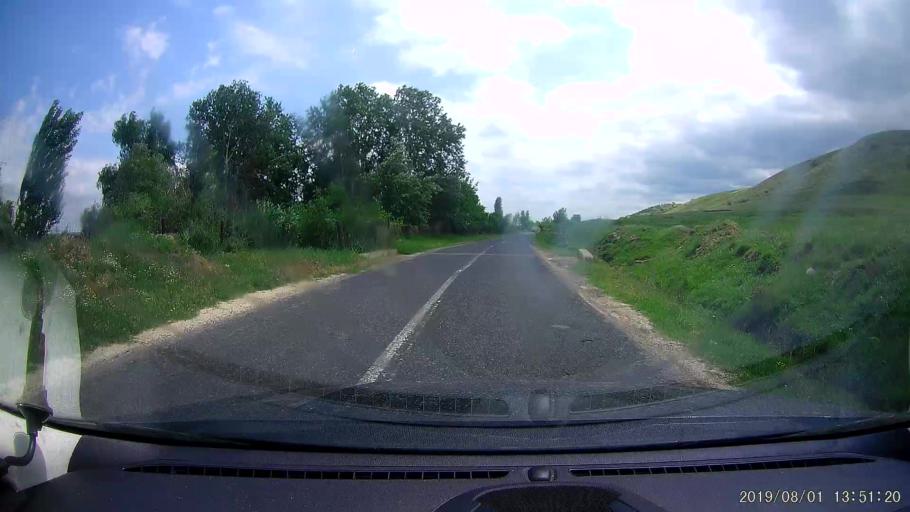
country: RO
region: Galati
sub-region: Comuna Vladesti
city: Vladesti
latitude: 45.8677
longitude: 28.0971
